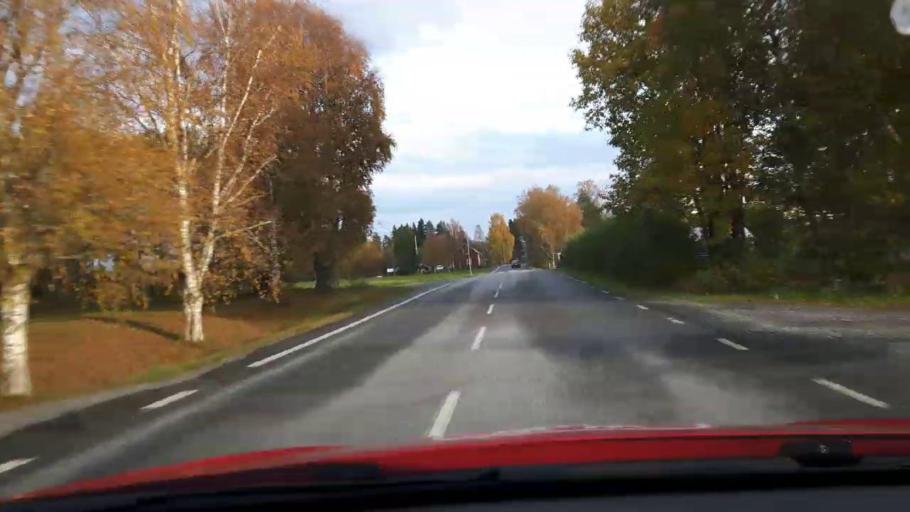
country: SE
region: Jaemtland
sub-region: Krokoms Kommun
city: Krokom
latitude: 63.3393
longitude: 14.5847
